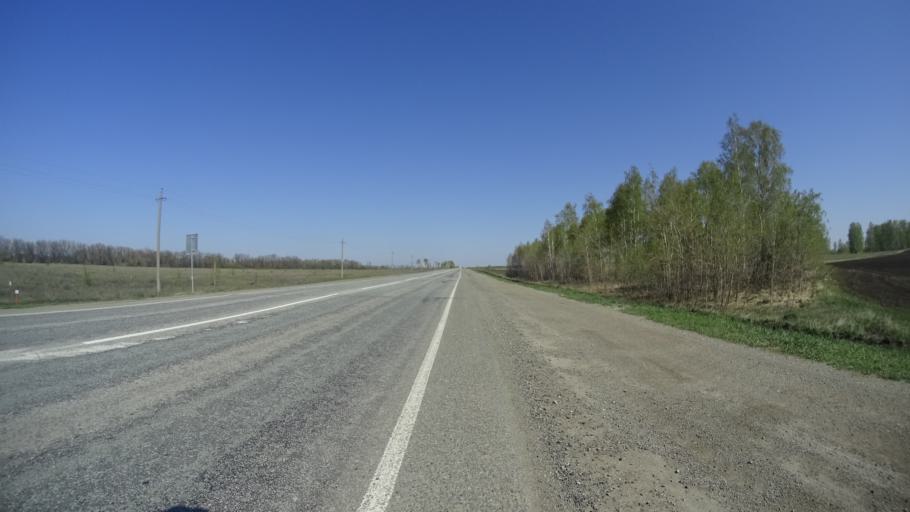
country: RU
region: Chelyabinsk
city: Troitsk
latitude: 54.1897
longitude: 61.4336
